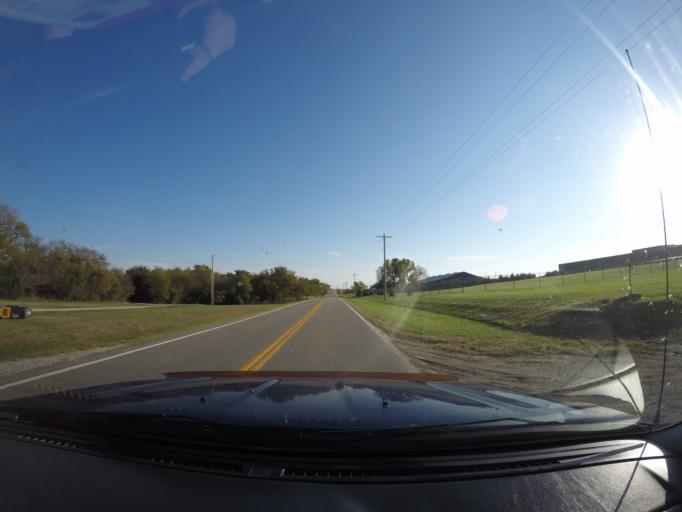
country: US
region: Kansas
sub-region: Saline County
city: Salina
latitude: 38.8512
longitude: -97.7613
